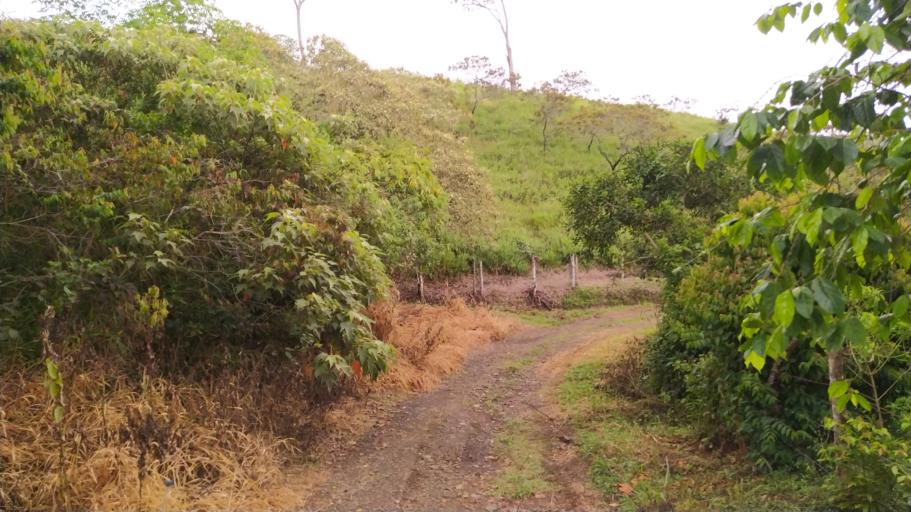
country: CO
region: Valle del Cauca
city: Jamundi
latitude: 3.3226
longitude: -76.5850
